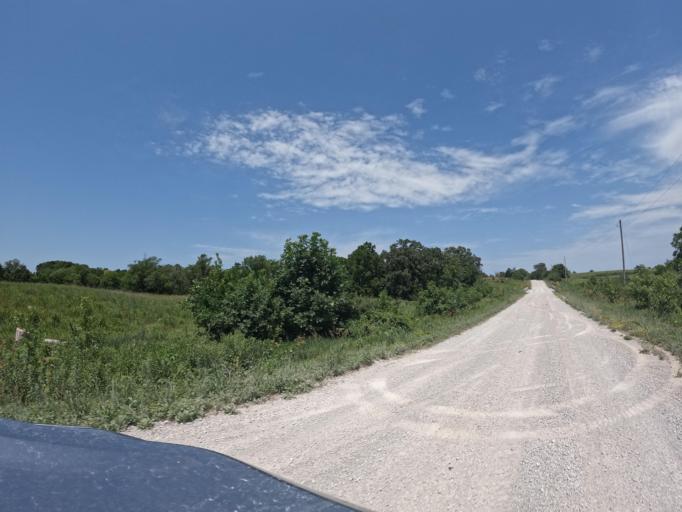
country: US
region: Iowa
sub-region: Appanoose County
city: Centerville
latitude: 40.8000
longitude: -92.9161
